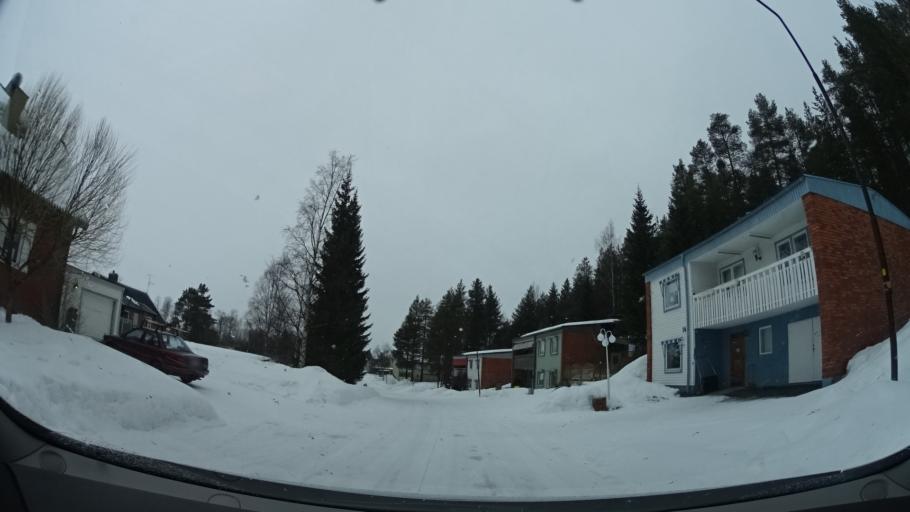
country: SE
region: Vaesterbotten
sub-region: Mala Kommun
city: Mala
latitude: 65.1787
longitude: 18.7496
